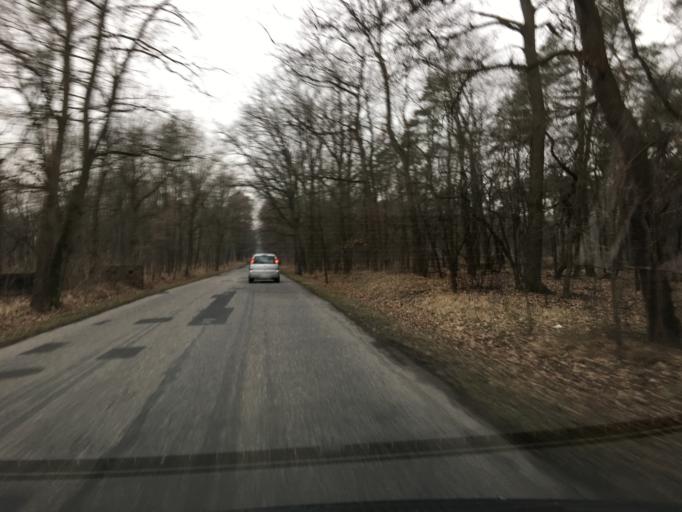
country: PL
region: Opole Voivodeship
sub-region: Powiat kedzierzynsko-kozielski
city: Kedzierzyn-Kozle
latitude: 50.3204
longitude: 18.2399
